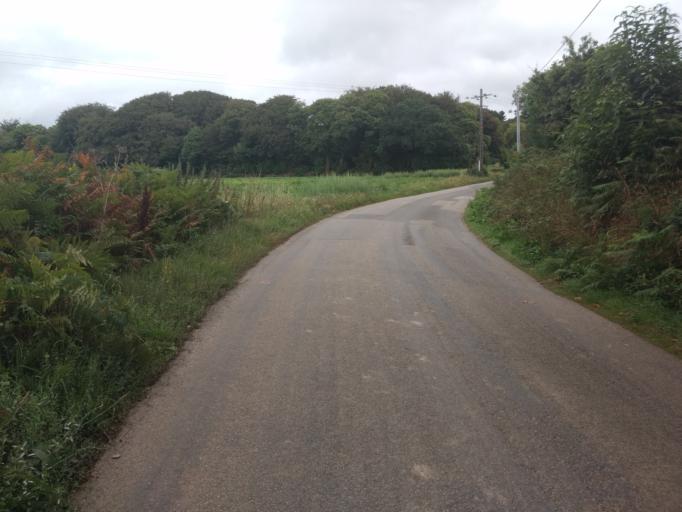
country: FR
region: Brittany
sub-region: Departement du Finistere
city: Loperhet
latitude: 48.3704
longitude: -4.2946
